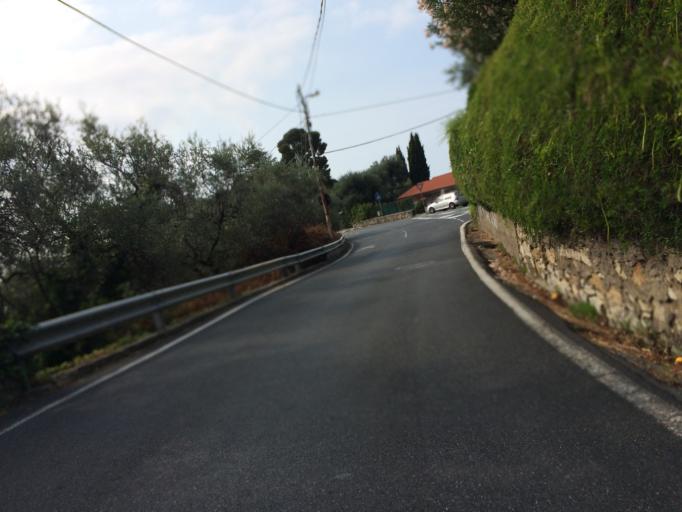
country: IT
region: Liguria
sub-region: Provincia di Imperia
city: San Remo
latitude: 43.8355
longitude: 7.7585
